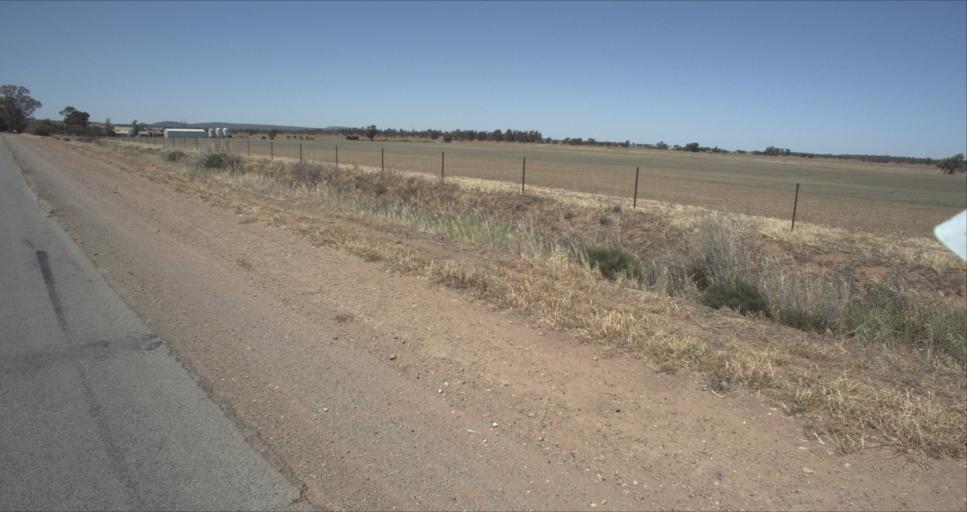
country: AU
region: New South Wales
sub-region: Leeton
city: Leeton
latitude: -34.5404
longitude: 146.4388
